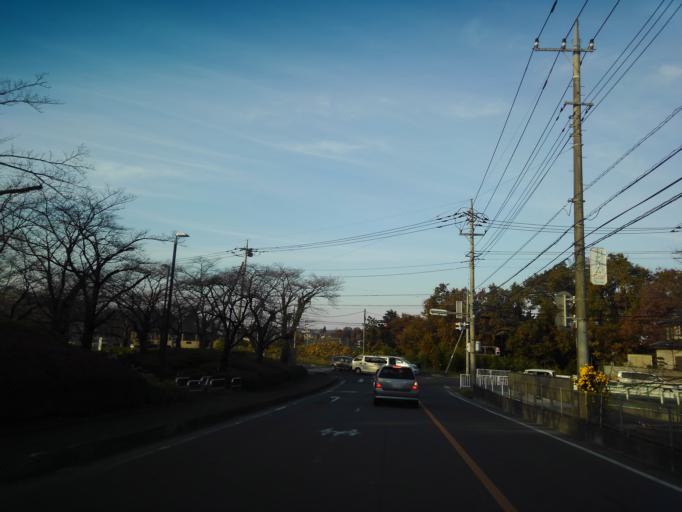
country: JP
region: Saitama
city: Hanno
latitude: 35.8336
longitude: 139.3362
